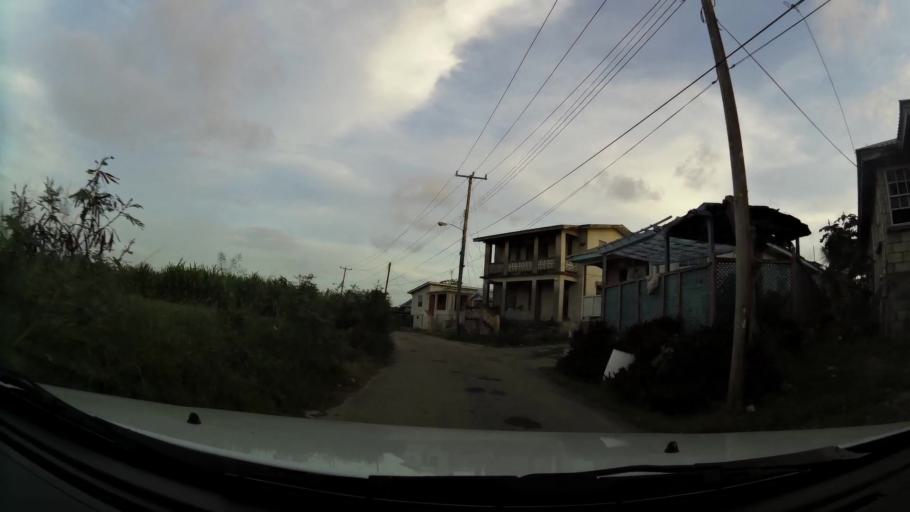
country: BB
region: Saint Philip
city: Crane
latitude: 13.0961
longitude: -59.4917
